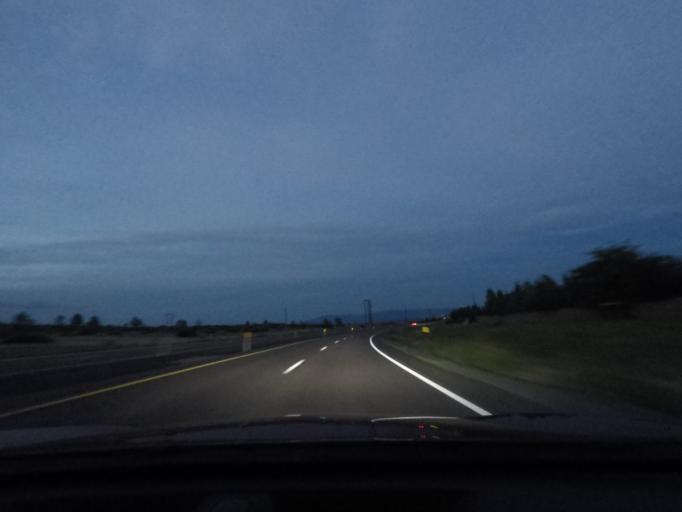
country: US
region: Arizona
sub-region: Yavapai County
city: Prescott
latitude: 34.6288
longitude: -112.4489
